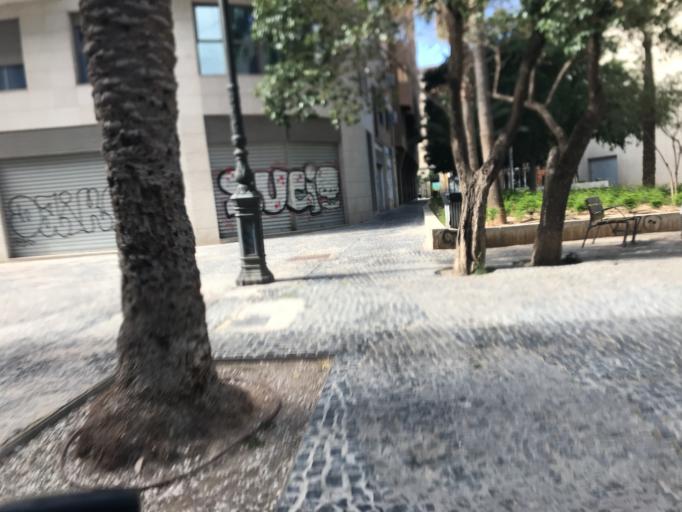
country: ES
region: Valencia
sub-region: Provincia de Valencia
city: Valencia
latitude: 39.4698
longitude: -0.3809
